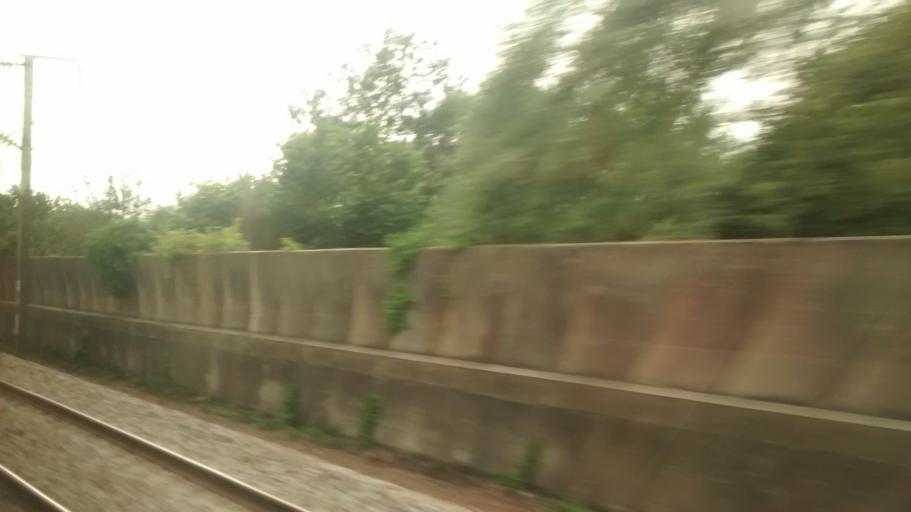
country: FR
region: Centre
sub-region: Departement d'Eure-et-Loir
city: Voves
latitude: 48.2546
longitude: 1.5710
